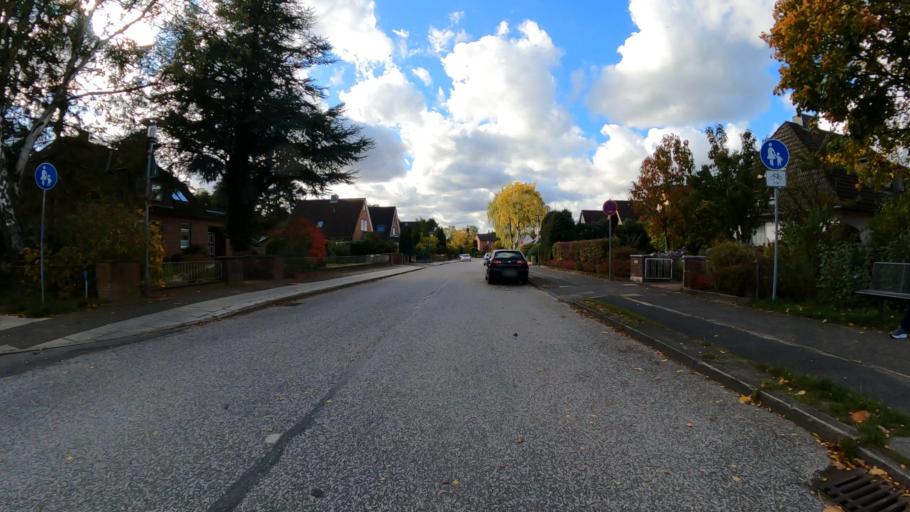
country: DE
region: Schleswig-Holstein
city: Ahrensburg
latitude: 53.6743
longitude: 10.2340
